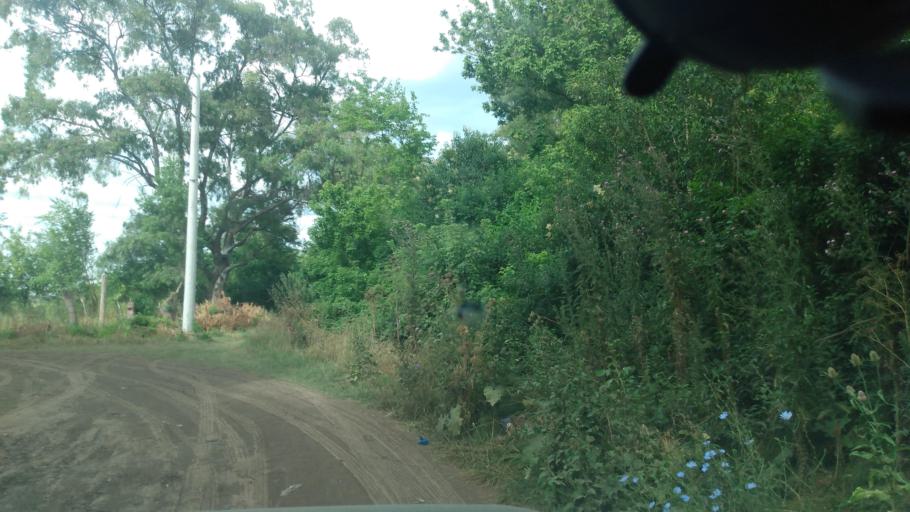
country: AR
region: Buenos Aires
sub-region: Partido de Lujan
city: Lujan
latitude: -34.5985
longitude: -59.0592
